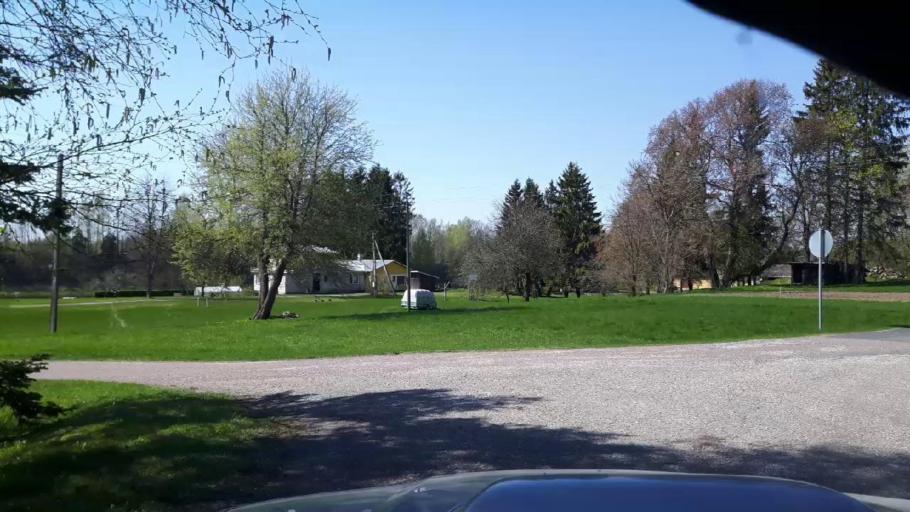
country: EE
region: Paernumaa
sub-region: Tootsi vald
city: Tootsi
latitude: 58.4643
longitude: 24.7749
